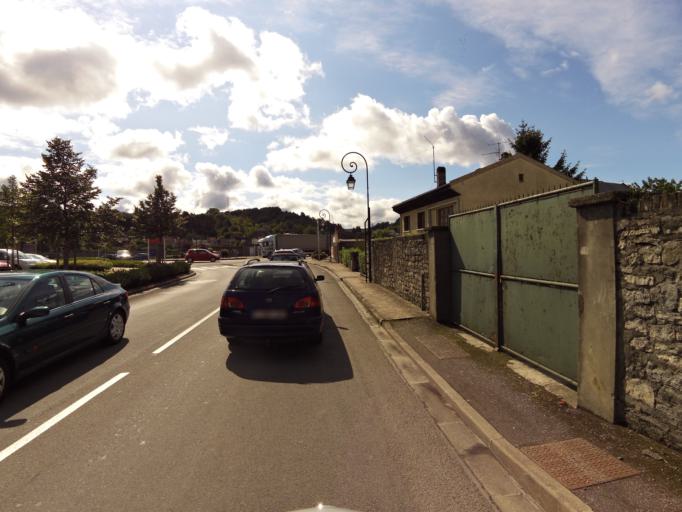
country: FR
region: Champagne-Ardenne
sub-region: Departement des Ardennes
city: Givet
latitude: 50.1353
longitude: 4.8205
